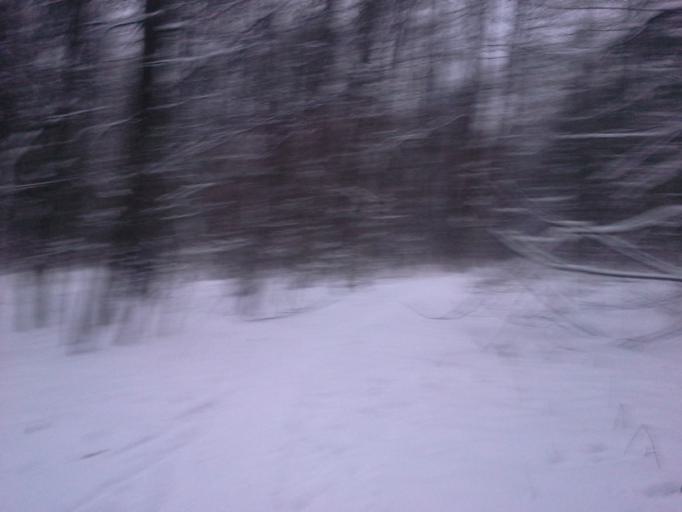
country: RU
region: Moskovskaya
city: Kommunarka
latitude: 55.5804
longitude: 37.4942
